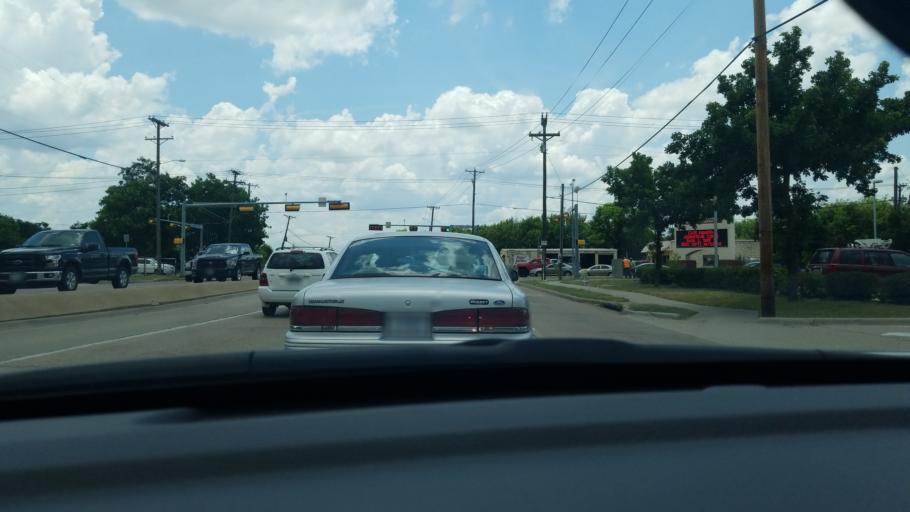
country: US
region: Texas
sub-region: Dallas County
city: Sunnyvale
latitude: 32.8147
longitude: -96.5960
